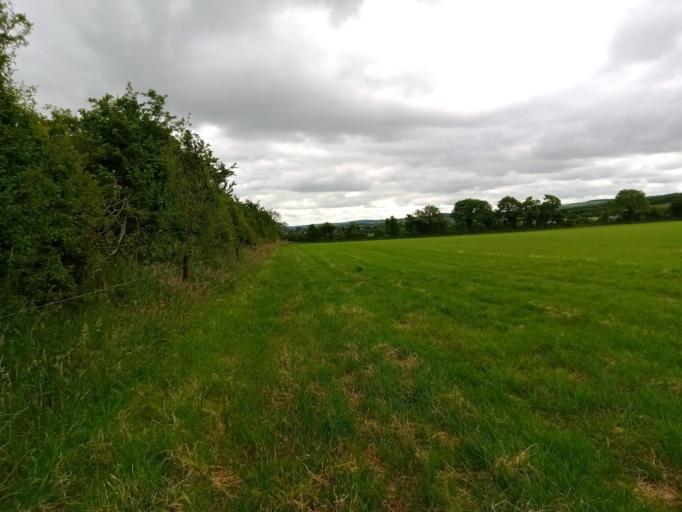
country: IE
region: Leinster
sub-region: Laois
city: Rathdowney
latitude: 52.7841
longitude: -7.4711
